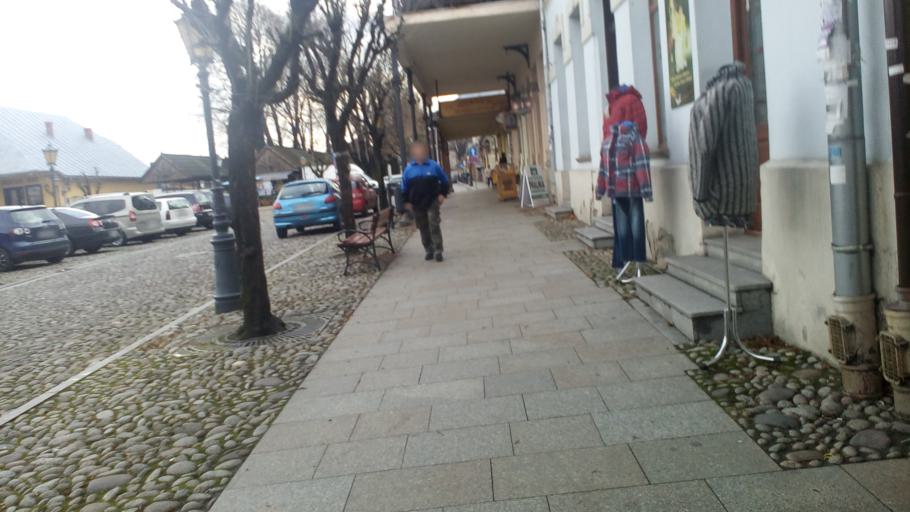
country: PL
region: Lesser Poland Voivodeship
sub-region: Powiat nowosadecki
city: Stary Sacz
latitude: 49.5635
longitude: 20.6350
